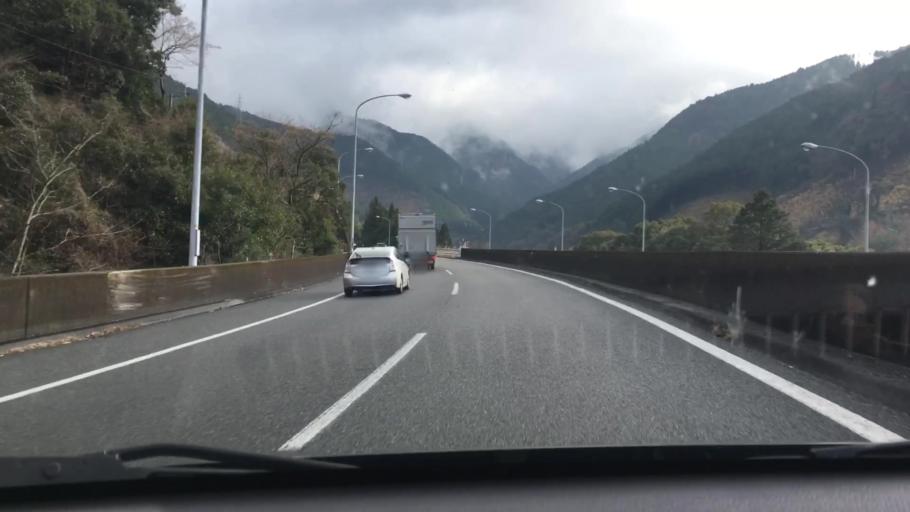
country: JP
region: Kumamoto
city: Yatsushiro
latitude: 32.4022
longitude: 130.6982
